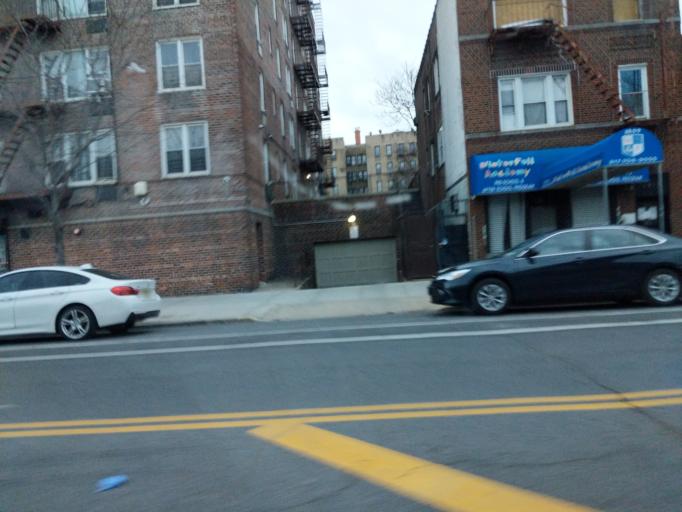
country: US
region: New York
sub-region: Bronx
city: The Bronx
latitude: 40.8366
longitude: -73.8523
